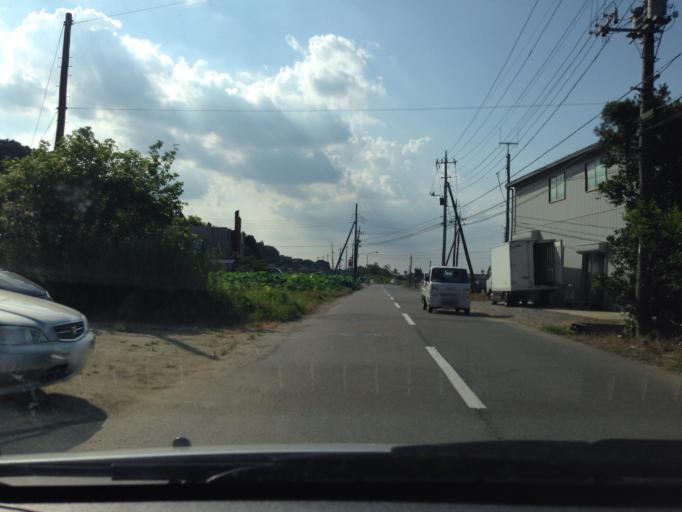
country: JP
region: Ibaraki
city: Ami
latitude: 36.0413
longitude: 140.2297
